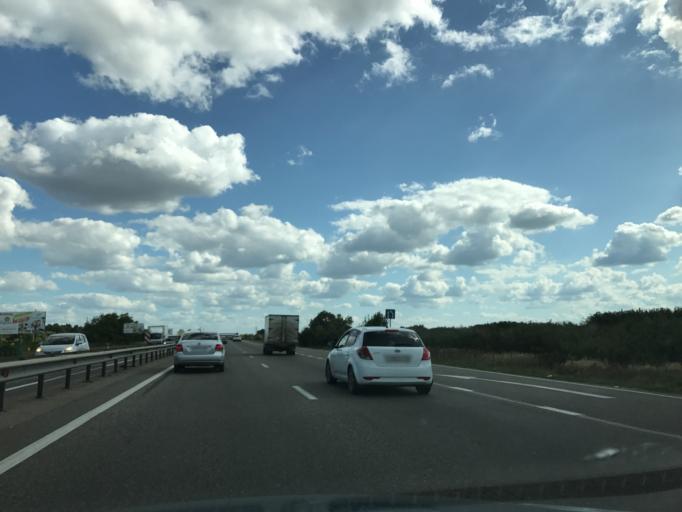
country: RU
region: Adygeya
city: Adygeysk
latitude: 44.9207
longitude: 39.1454
